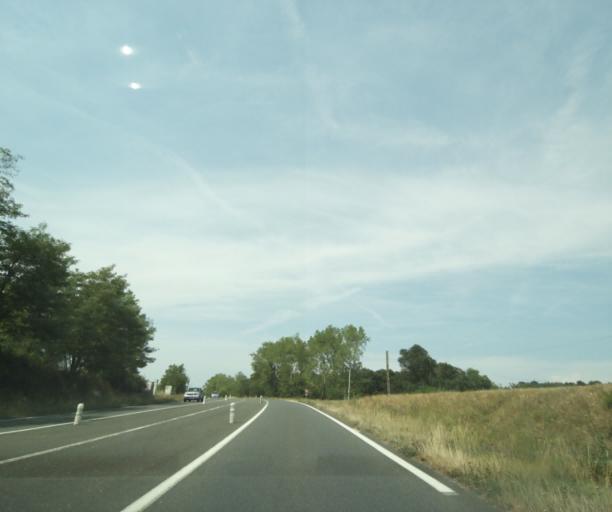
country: FR
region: Centre
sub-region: Departement d'Indre-et-Loire
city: Sainte-Maure-de-Touraine
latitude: 47.1449
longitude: 0.6468
